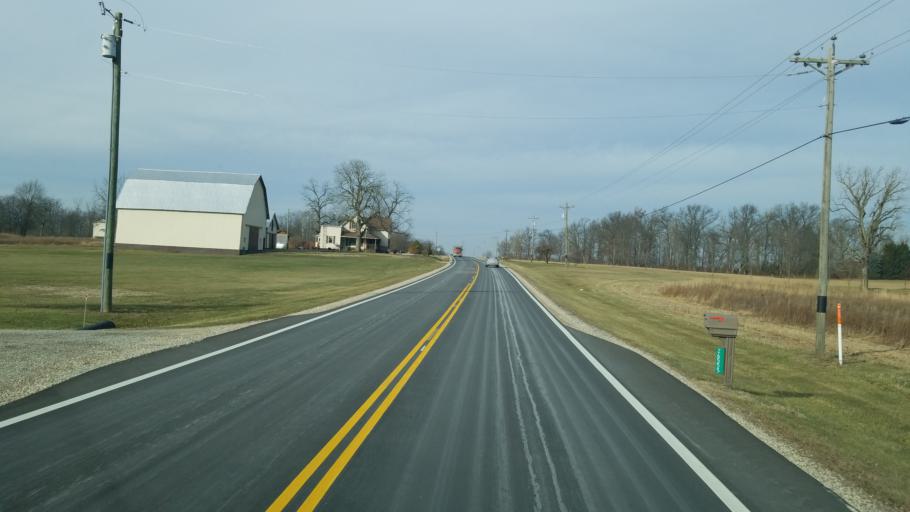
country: US
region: Ohio
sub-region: Union County
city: Richwood
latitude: 40.3857
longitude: -83.4066
